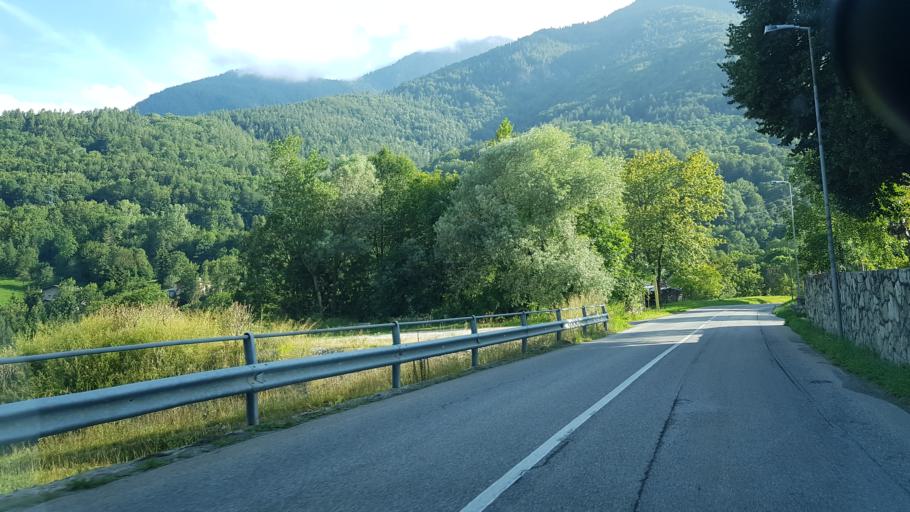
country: IT
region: Piedmont
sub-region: Provincia di Cuneo
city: Sampeyre
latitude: 44.5768
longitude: 7.1982
